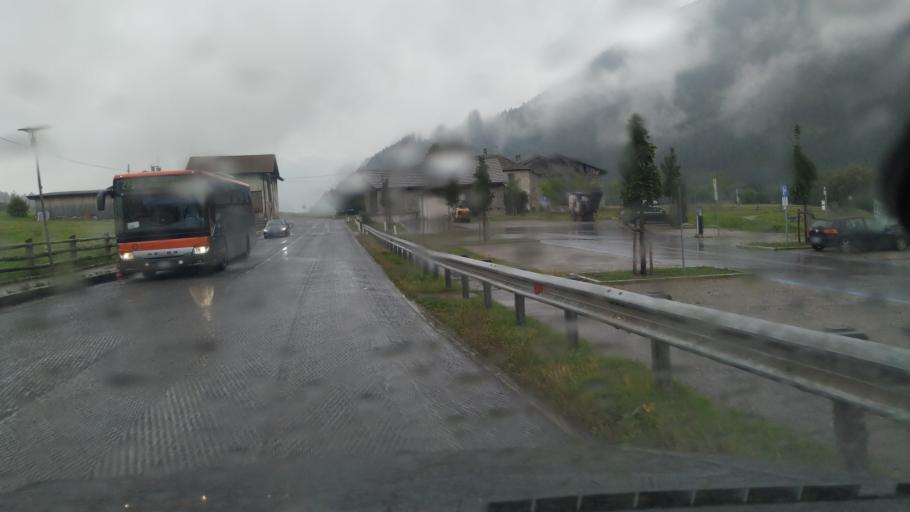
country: IT
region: Trentino-Alto Adige
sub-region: Bolzano
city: Curon Venosta
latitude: 46.7496
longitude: 10.5358
